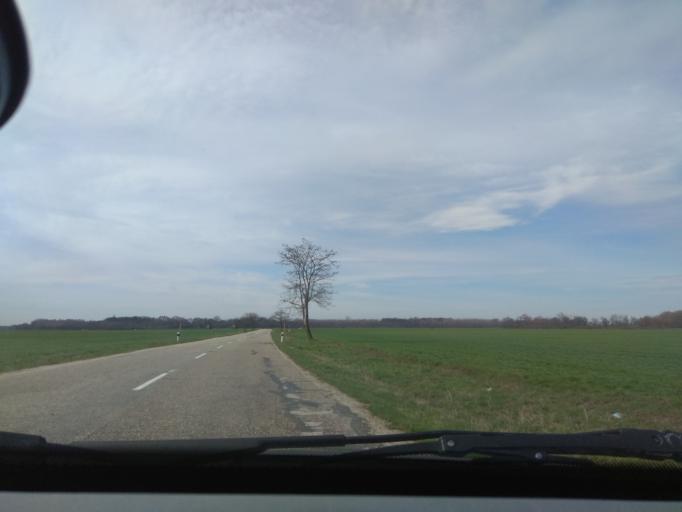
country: SK
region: Trnavsky
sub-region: Okres Dunajska Streda
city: Velky Meder
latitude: 47.8295
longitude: 17.7541
